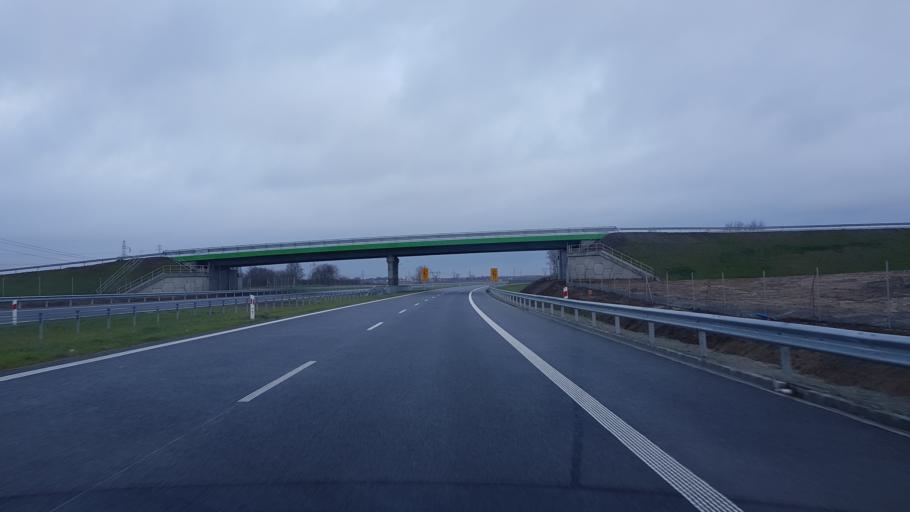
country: PL
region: West Pomeranian Voivodeship
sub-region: Koszalin
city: Koszalin
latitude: 54.2228
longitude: 16.1631
